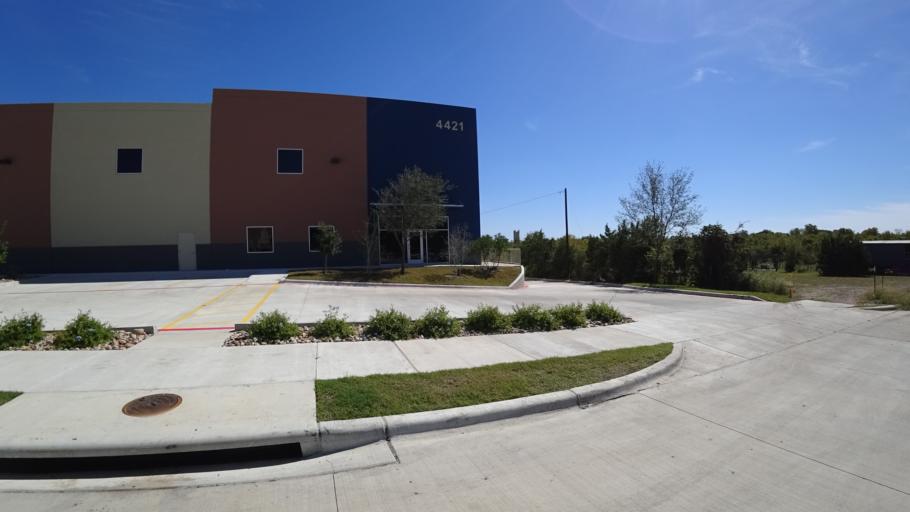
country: US
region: Texas
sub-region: Travis County
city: Austin
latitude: 30.1937
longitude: -97.7057
